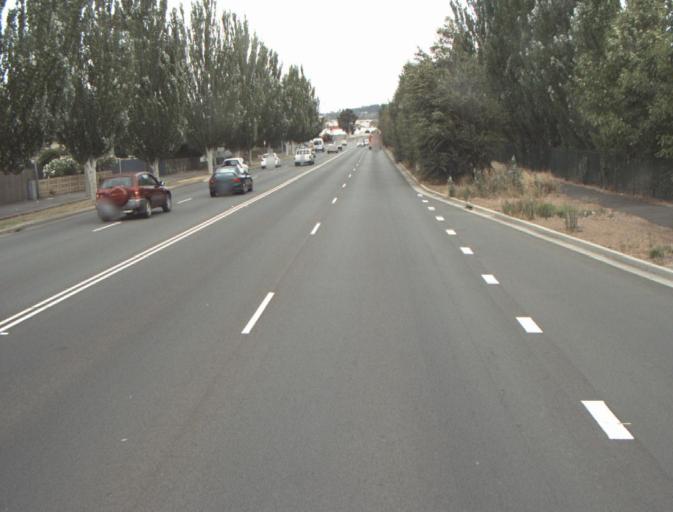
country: AU
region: Tasmania
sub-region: Launceston
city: Launceston
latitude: -41.4281
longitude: 147.1321
